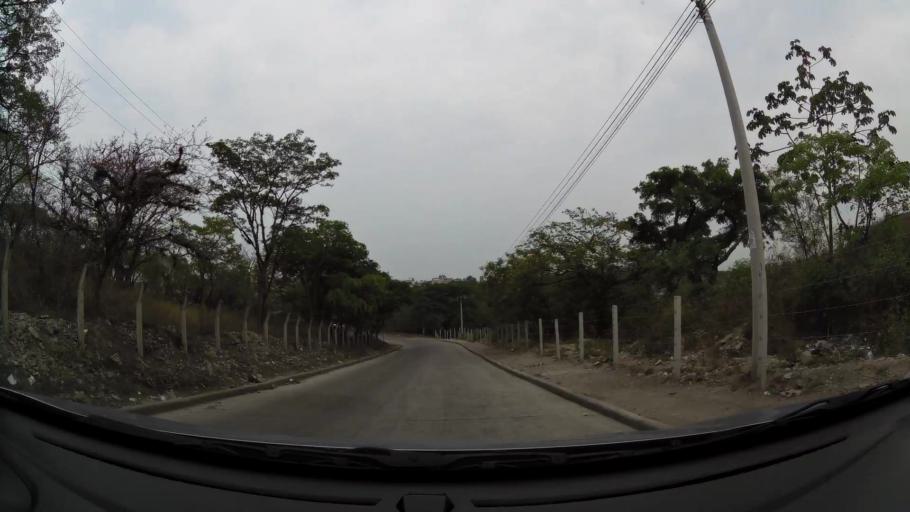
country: HN
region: Francisco Morazan
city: Tegucigalpa
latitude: 14.0689
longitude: -87.2382
